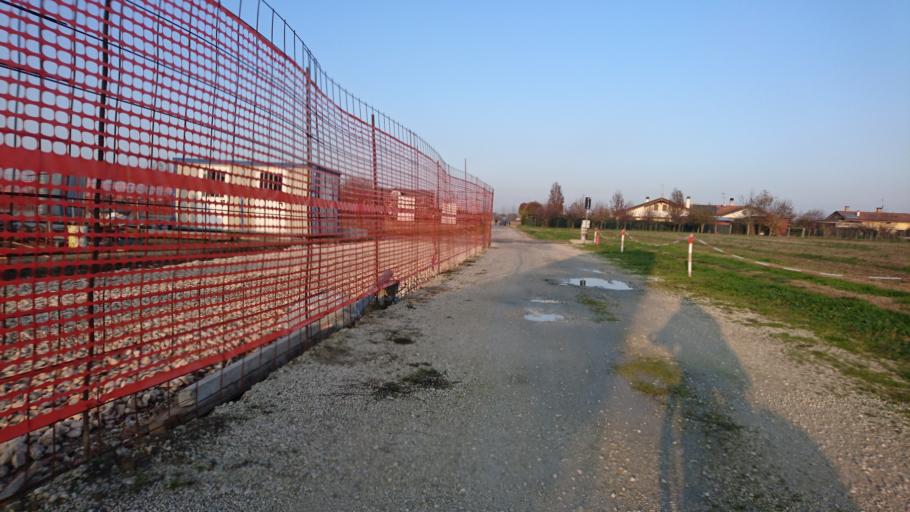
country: IT
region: Veneto
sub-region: Provincia di Padova
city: Legnaro
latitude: 45.3350
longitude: 11.9517
